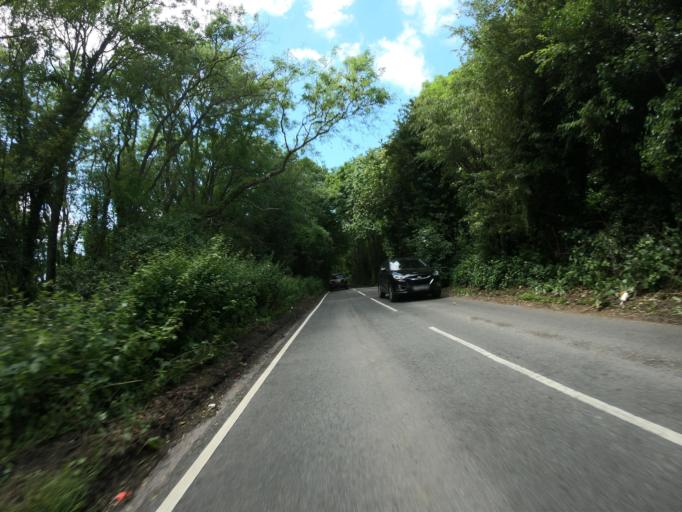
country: GB
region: England
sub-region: Kent
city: Halstead
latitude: 51.3073
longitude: 0.1406
